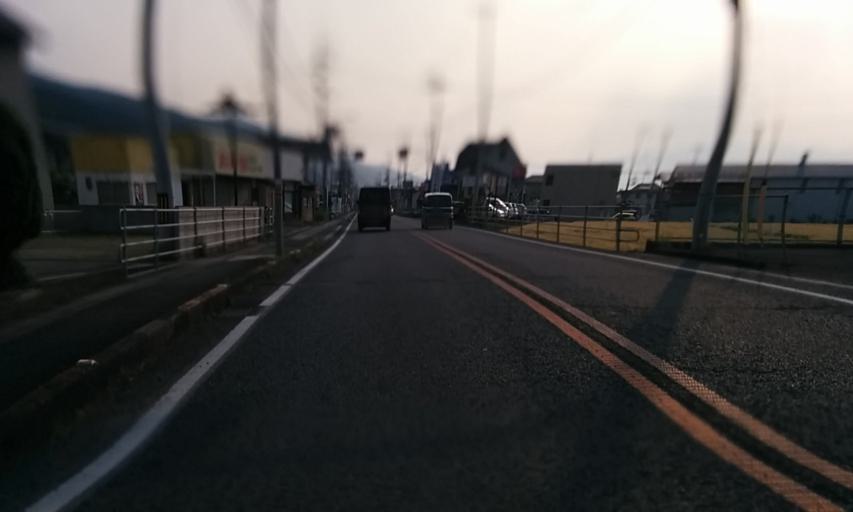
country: JP
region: Ehime
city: Saijo
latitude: 33.8983
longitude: 133.1741
